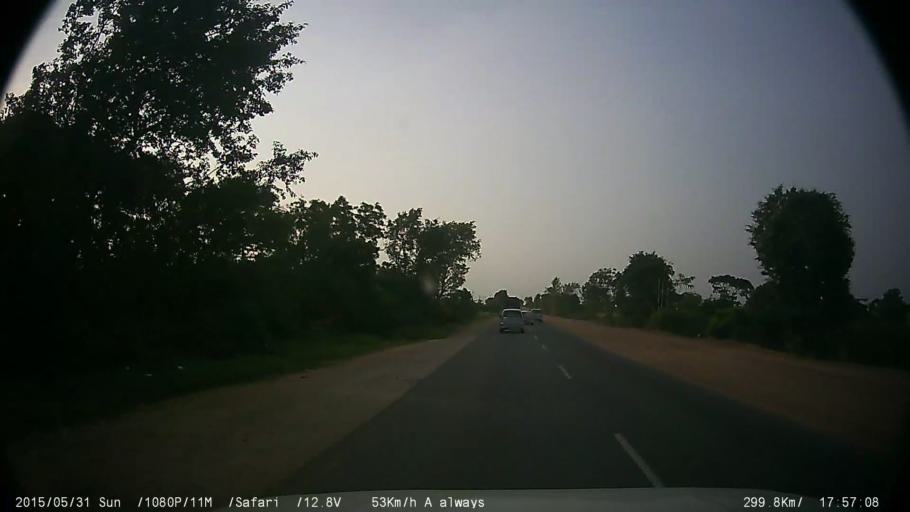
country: IN
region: Karnataka
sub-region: Mysore
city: Nanjangud
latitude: 11.9988
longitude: 76.6694
